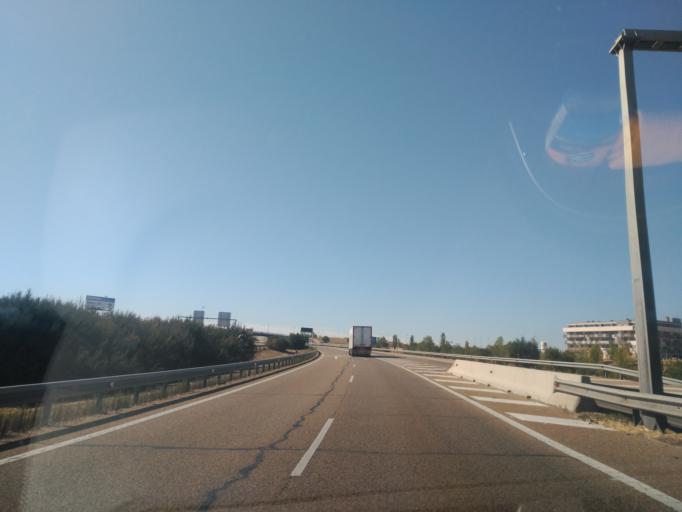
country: ES
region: Castille and Leon
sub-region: Provincia de Valladolid
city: Arroyo
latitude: 41.6241
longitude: -4.7881
